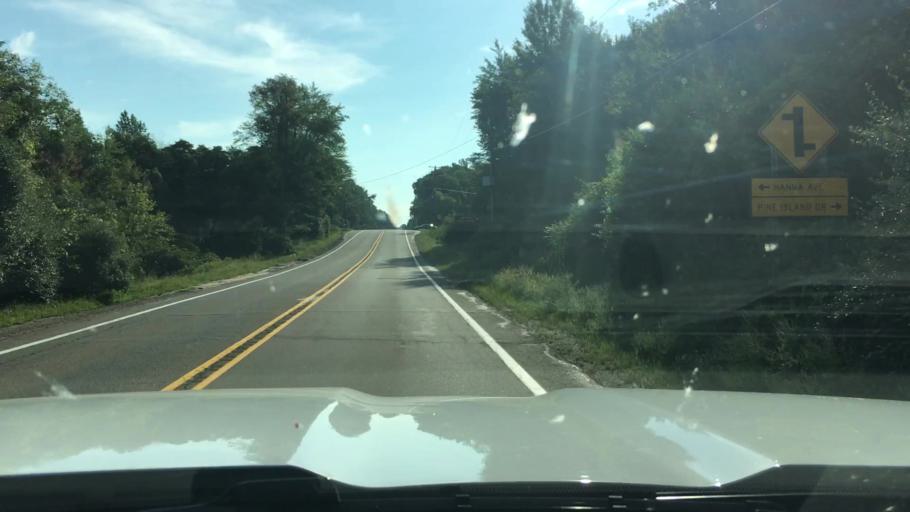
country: US
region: Michigan
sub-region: Kent County
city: Sparta
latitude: 43.2194
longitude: -85.6438
